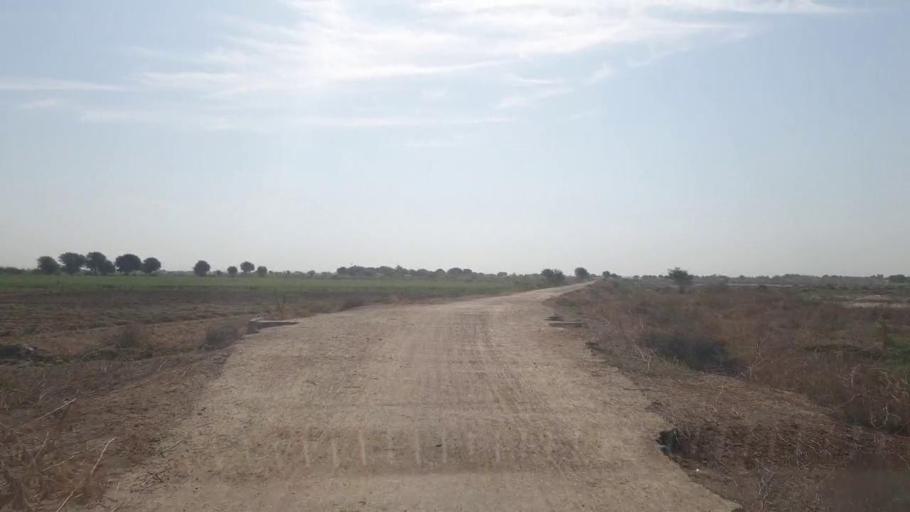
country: PK
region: Sindh
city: Umarkot
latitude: 25.2800
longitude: 69.6612
